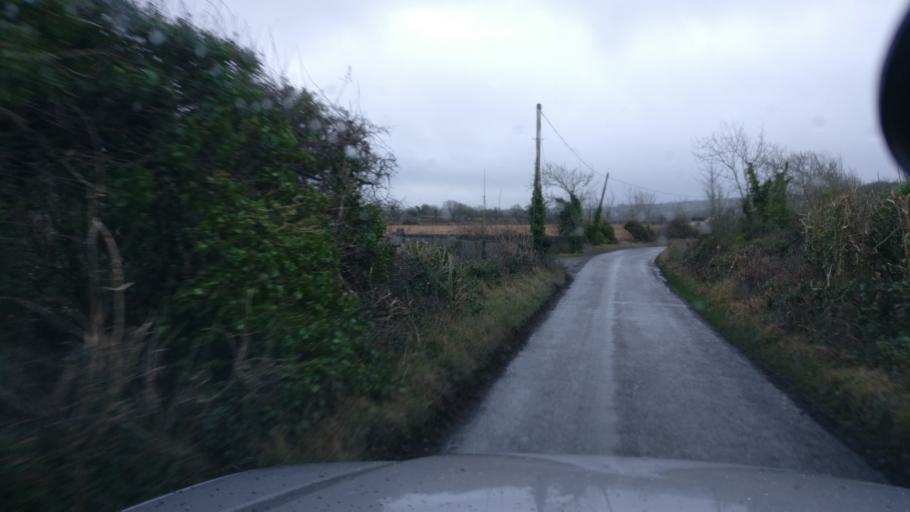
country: IE
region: Connaught
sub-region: County Galway
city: Loughrea
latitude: 53.1980
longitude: -8.6635
